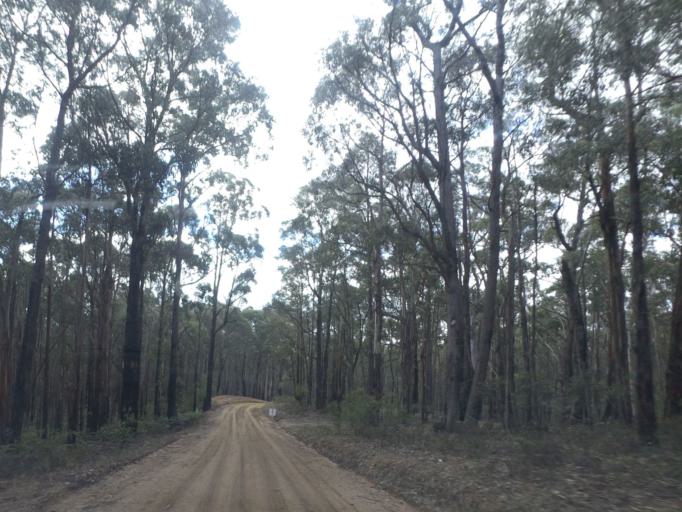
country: AU
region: Victoria
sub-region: Moorabool
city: Bacchus Marsh
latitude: -37.4563
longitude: 144.4706
